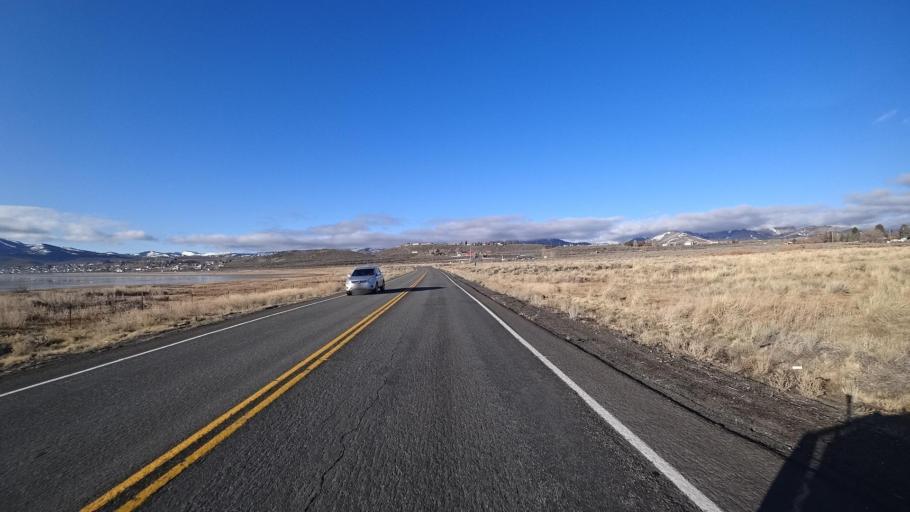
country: US
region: Nevada
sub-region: Washoe County
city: Cold Springs
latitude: 39.6712
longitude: -119.9906
